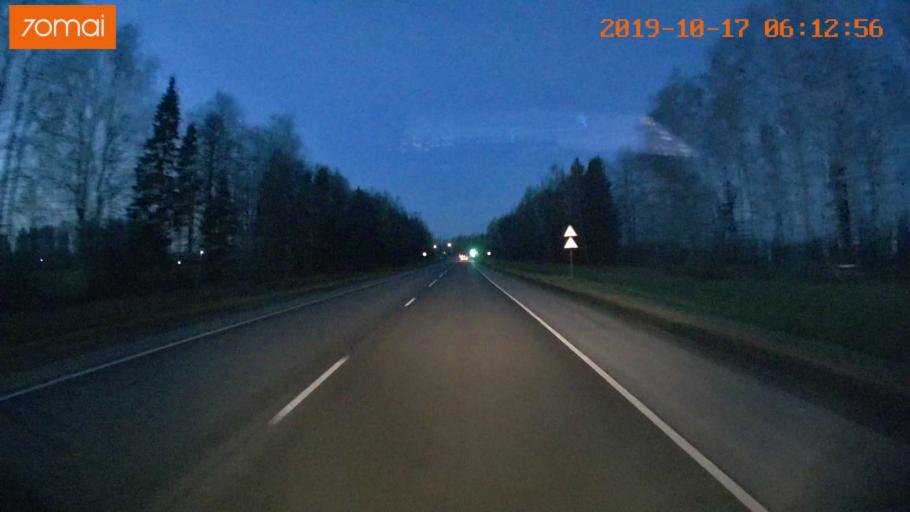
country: RU
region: Ivanovo
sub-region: Gorod Ivanovo
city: Ivanovo
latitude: 56.9043
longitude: 40.9403
